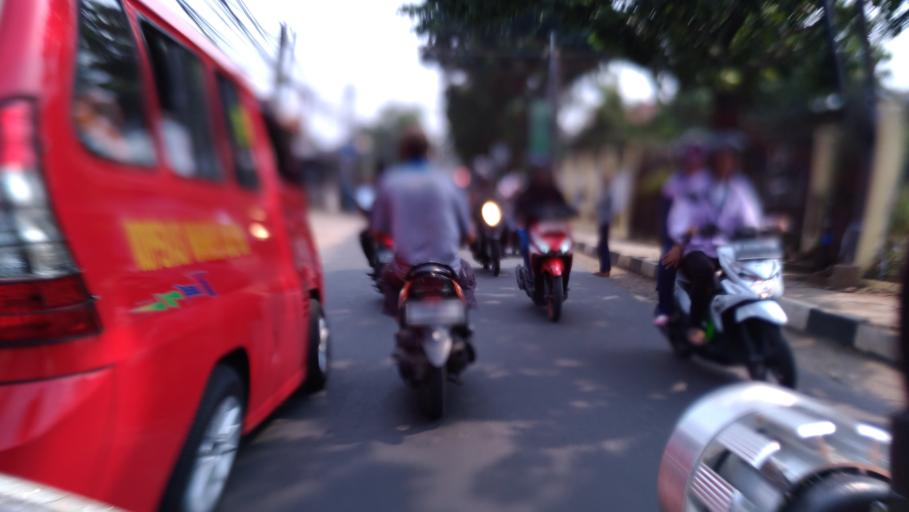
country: ID
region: West Java
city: Depok
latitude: -6.3517
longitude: 106.8809
